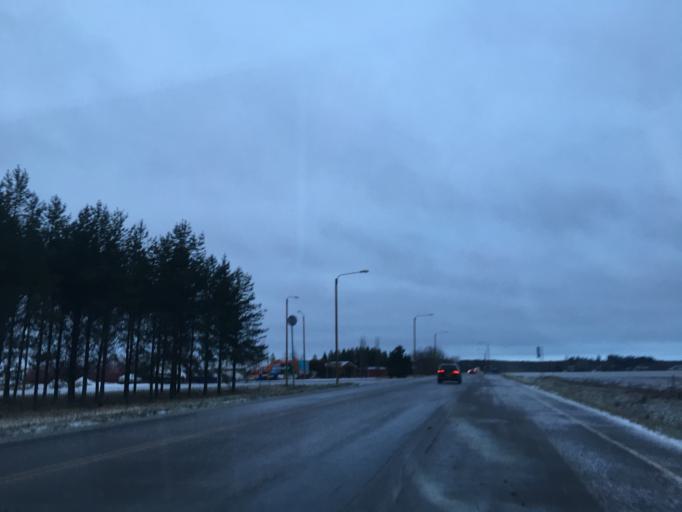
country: FI
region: Varsinais-Suomi
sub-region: Loimaa
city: Aura
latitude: 60.6554
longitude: 22.5937
